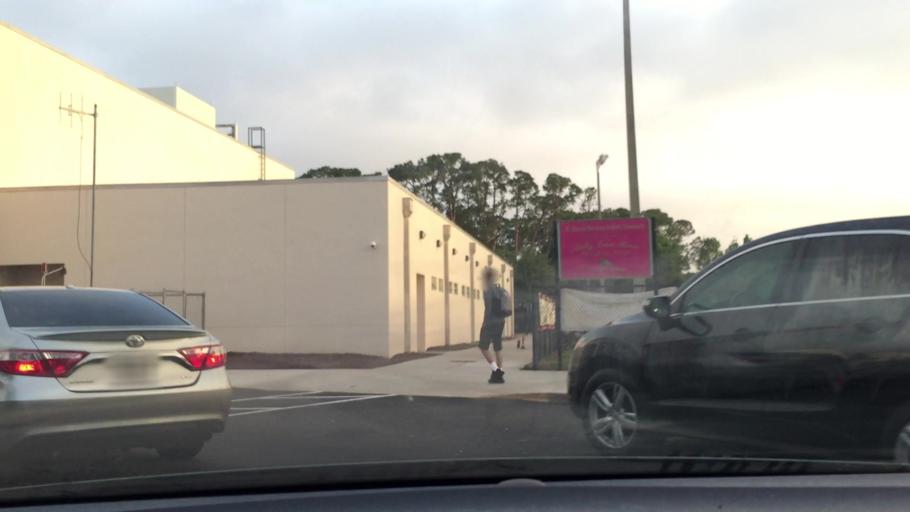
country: US
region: Florida
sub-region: Orange County
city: Fairview Shores
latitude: 28.5879
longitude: -81.3910
